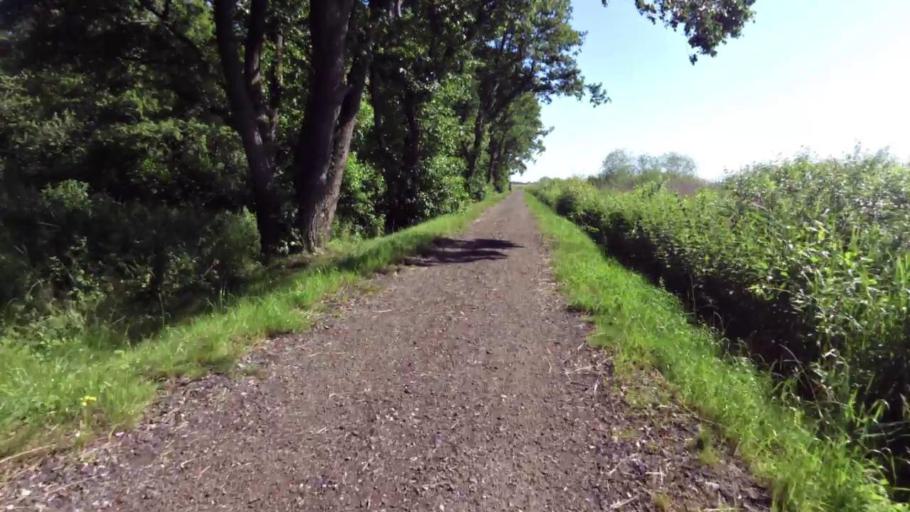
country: PL
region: West Pomeranian Voivodeship
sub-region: Powiat koszalinski
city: Mielno
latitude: 54.2701
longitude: 16.1102
